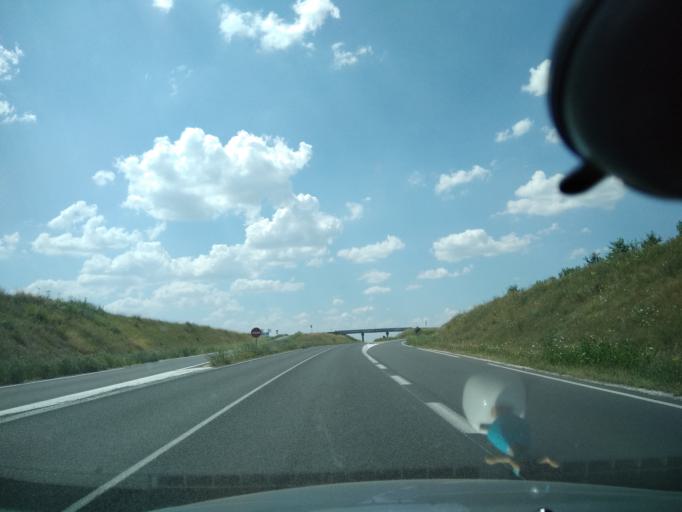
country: FR
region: Centre
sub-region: Departement d'Indre-et-Loire
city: Blere
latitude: 47.3151
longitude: 0.9918
